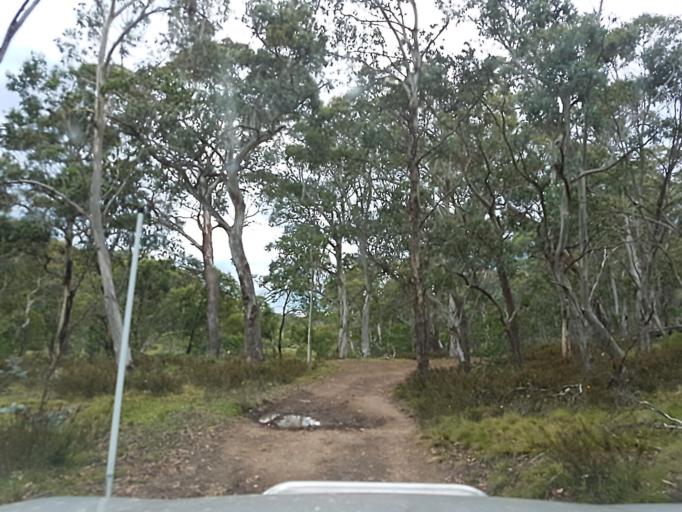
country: AU
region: New South Wales
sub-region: Snowy River
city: Jindabyne
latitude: -36.8865
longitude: 148.1307
